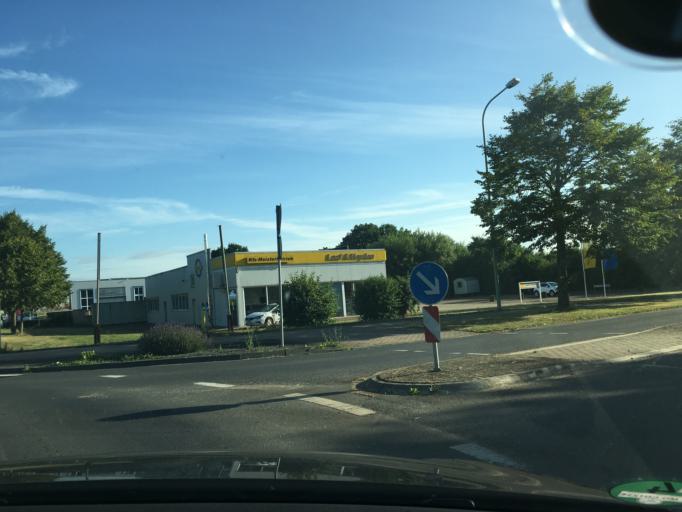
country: DE
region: North Rhine-Westphalia
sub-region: Regierungsbezirk Koln
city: Niederzier
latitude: 50.8721
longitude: 6.4735
